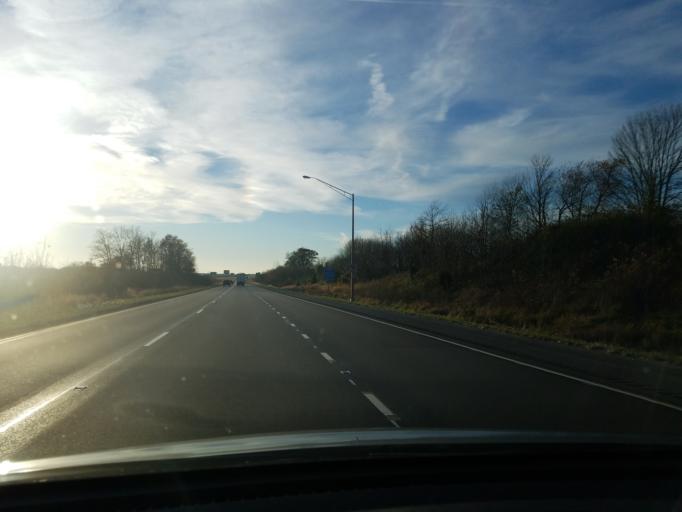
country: US
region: Indiana
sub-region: Spencer County
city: Dale
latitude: 38.1960
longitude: -86.9535
